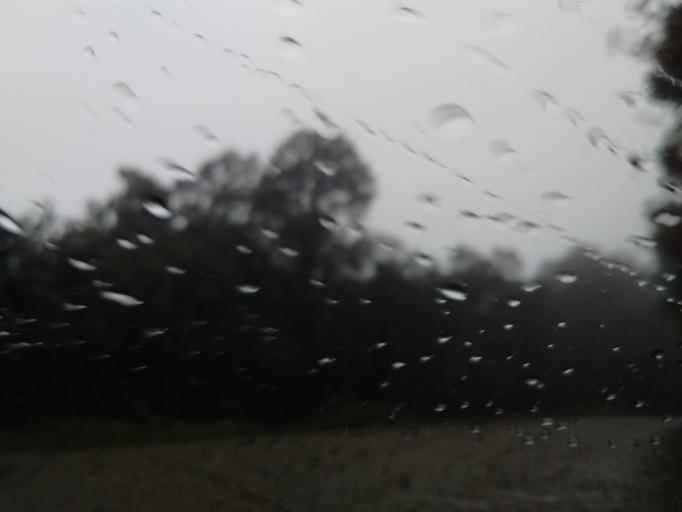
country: CO
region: Cauca
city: Paispamba
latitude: 2.1654
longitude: -76.4123
